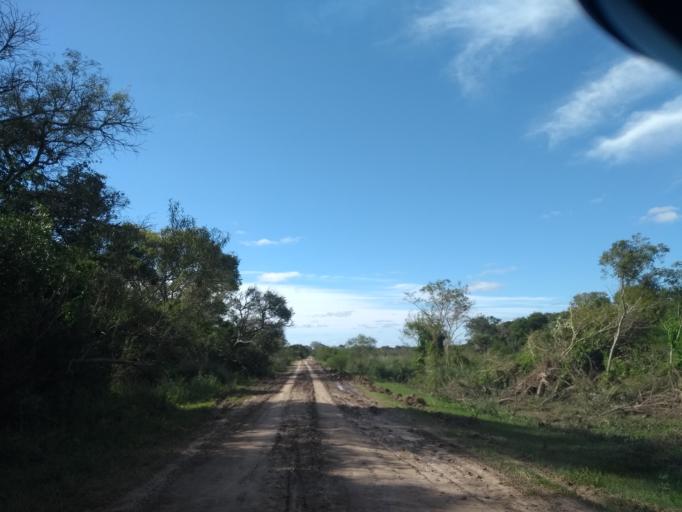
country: AR
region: Chaco
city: Margarita Belen
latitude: -27.2825
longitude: -58.9261
